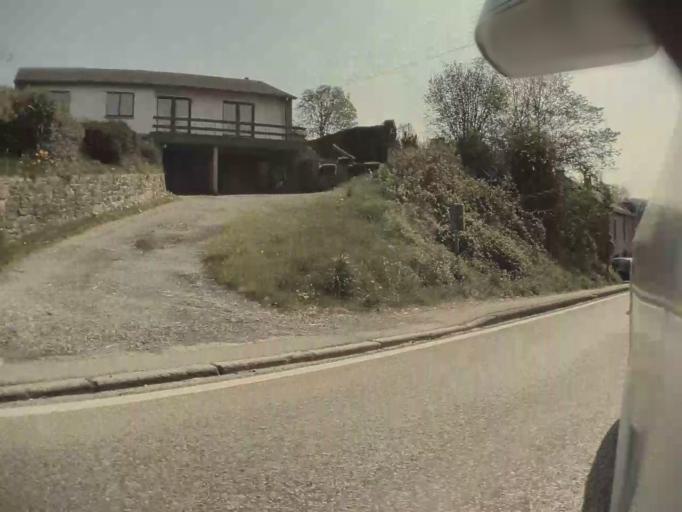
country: BE
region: Wallonia
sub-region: Province de Namur
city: Dinant
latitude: 50.2668
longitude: 4.9241
